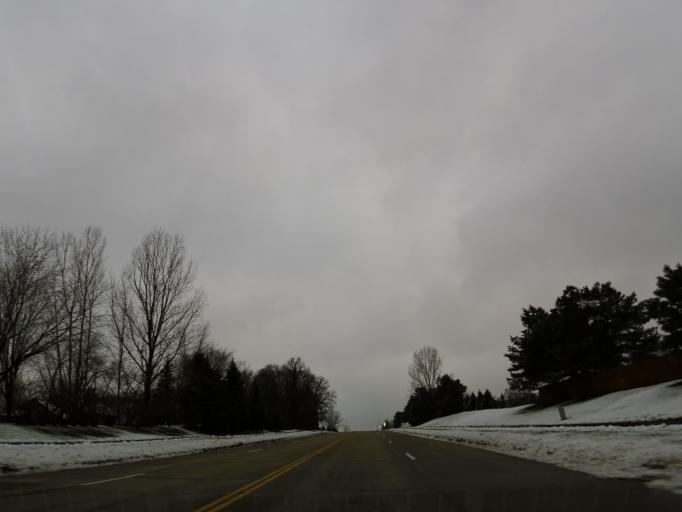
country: US
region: Minnesota
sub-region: Dakota County
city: Apple Valley
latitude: 44.6989
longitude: -93.2379
